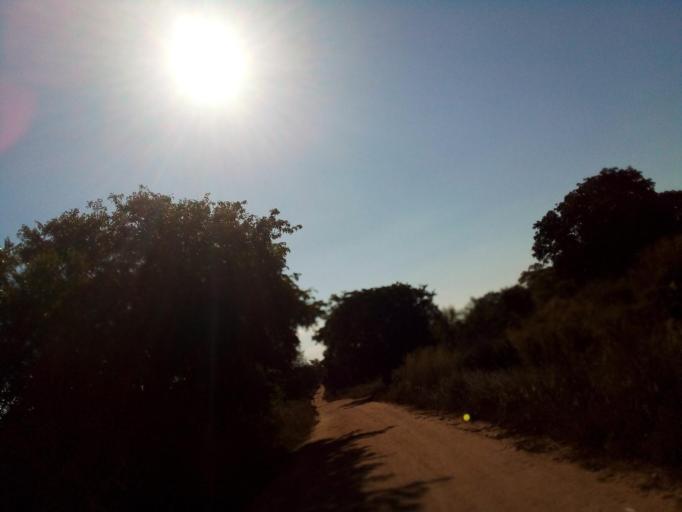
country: MZ
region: Zambezia
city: Quelimane
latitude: -17.5081
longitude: 36.5907
